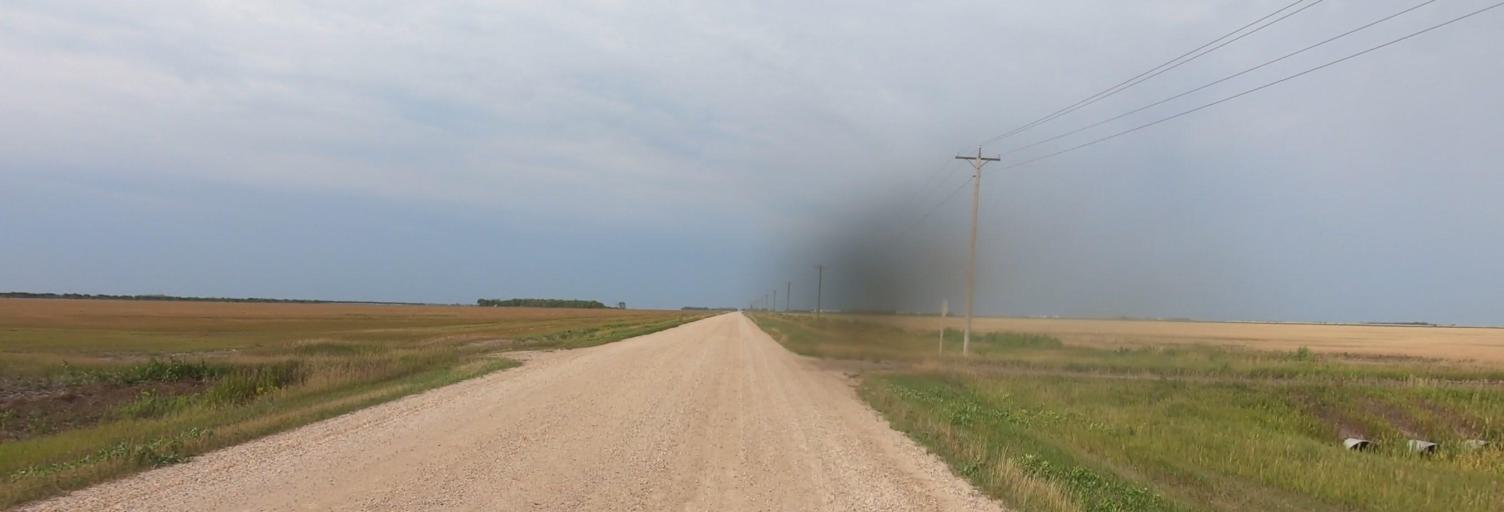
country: CA
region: Manitoba
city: Morris
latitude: 49.5764
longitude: -97.2996
